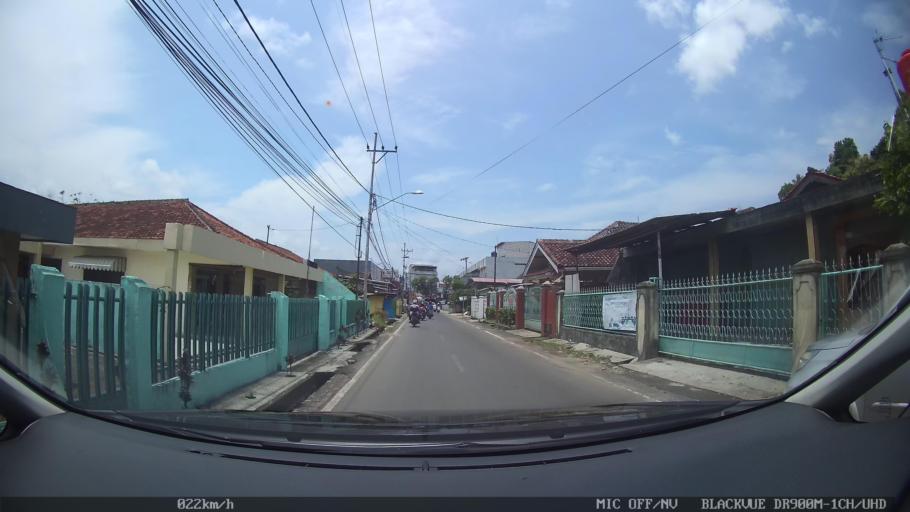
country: ID
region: Lampung
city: Kedaton
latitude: -5.3886
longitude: 105.2601
